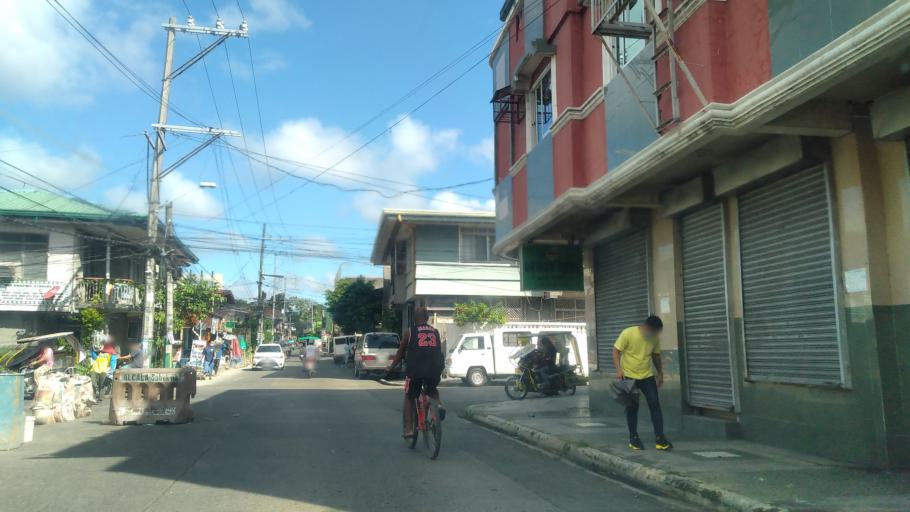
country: PH
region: Calabarzon
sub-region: Province of Quezon
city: Lucena
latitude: 13.9384
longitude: 121.6119
